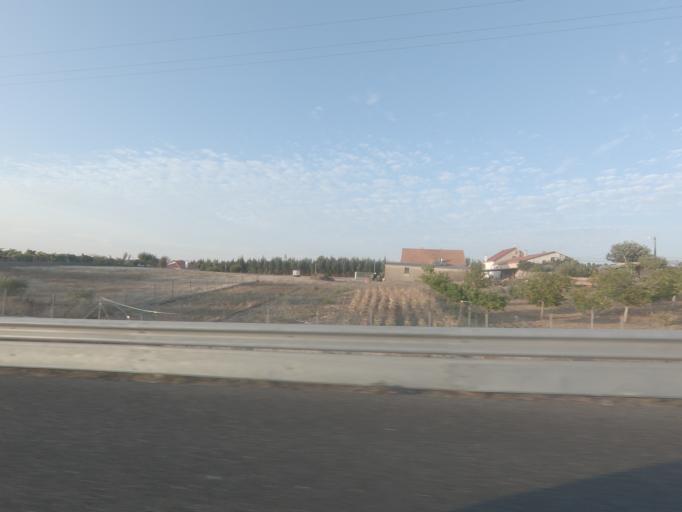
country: PT
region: Leiria
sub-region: Leiria
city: Santa Catarina da Serra
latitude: 39.7018
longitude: -8.6991
